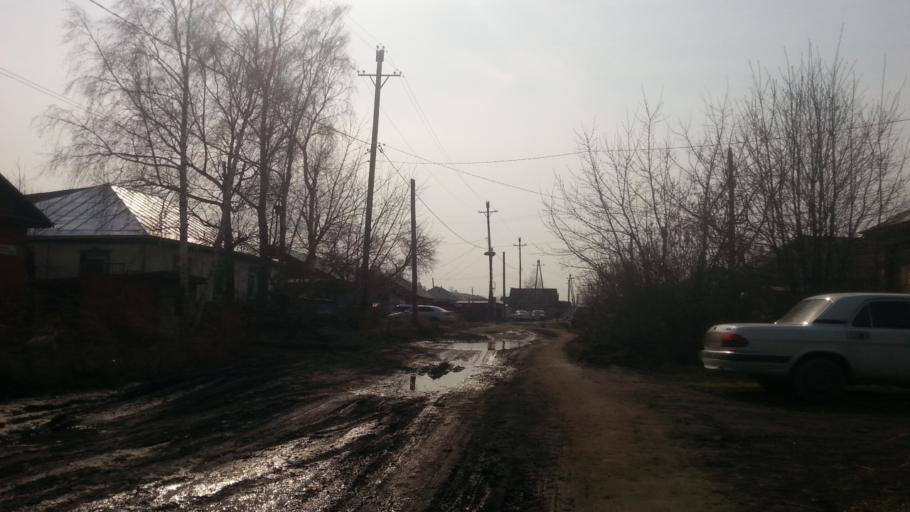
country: RU
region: Altai Krai
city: Zaton
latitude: 53.3212
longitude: 83.7772
